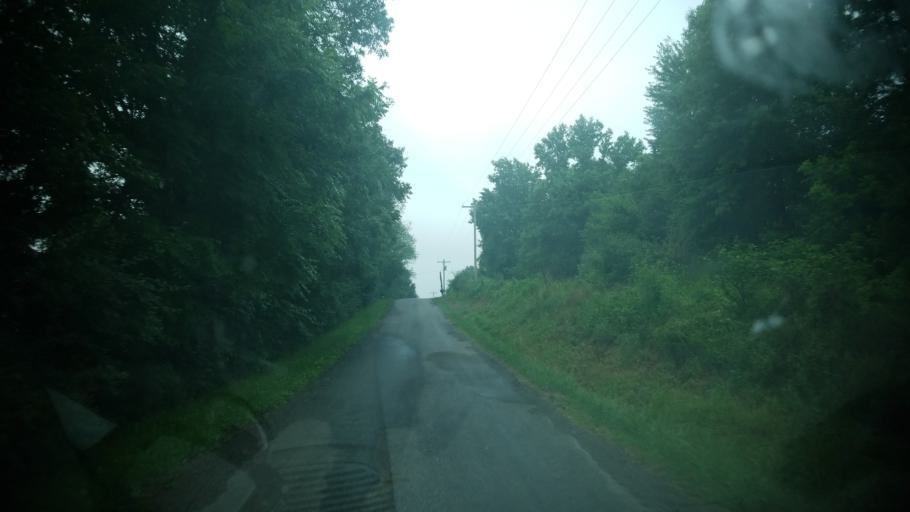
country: US
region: Illinois
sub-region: Clay County
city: Flora
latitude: 38.5591
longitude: -88.4030
